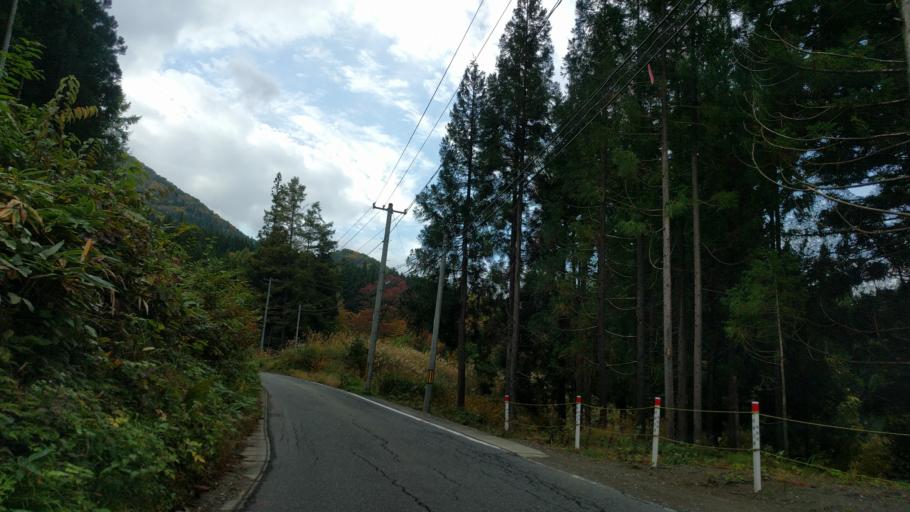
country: JP
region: Fukushima
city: Kitakata
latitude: 37.4002
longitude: 139.6954
